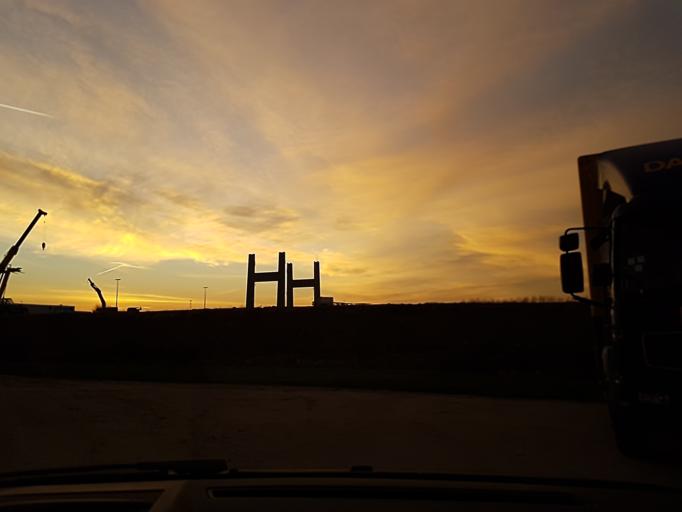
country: BE
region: Flanders
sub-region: Provincie Antwerpen
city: Willebroek
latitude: 51.0438
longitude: 4.3662
